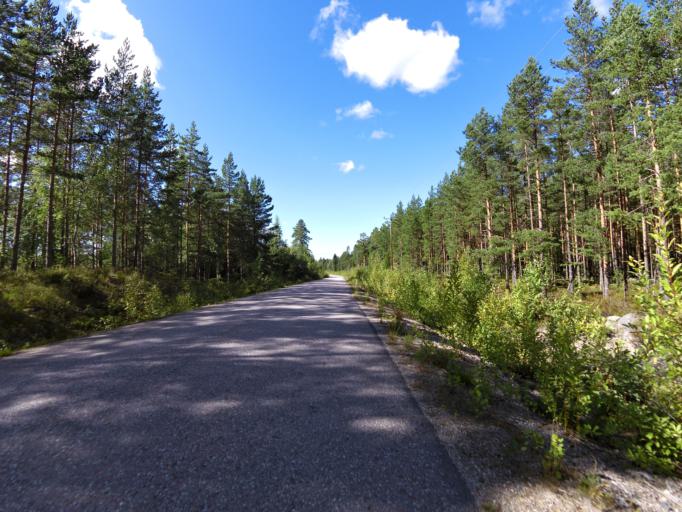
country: SE
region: Gaevleborg
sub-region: Gavle Kommun
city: Valbo
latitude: 60.7681
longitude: 16.9592
